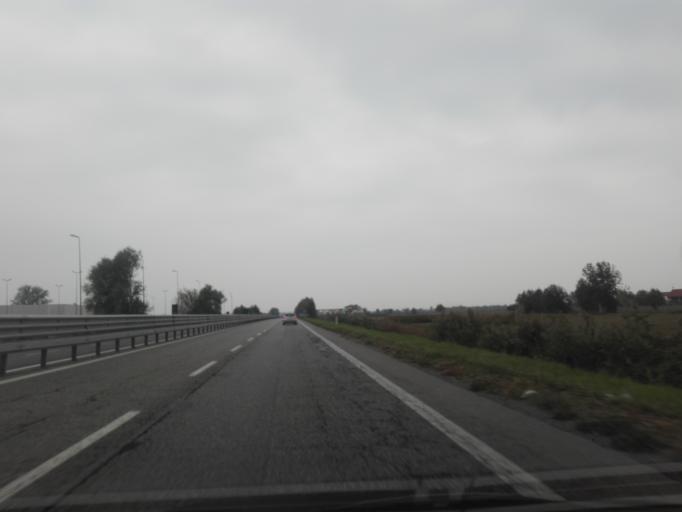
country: IT
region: Veneto
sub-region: Provincia di Verona
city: Isola Rizza
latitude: 45.2878
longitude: 11.1871
